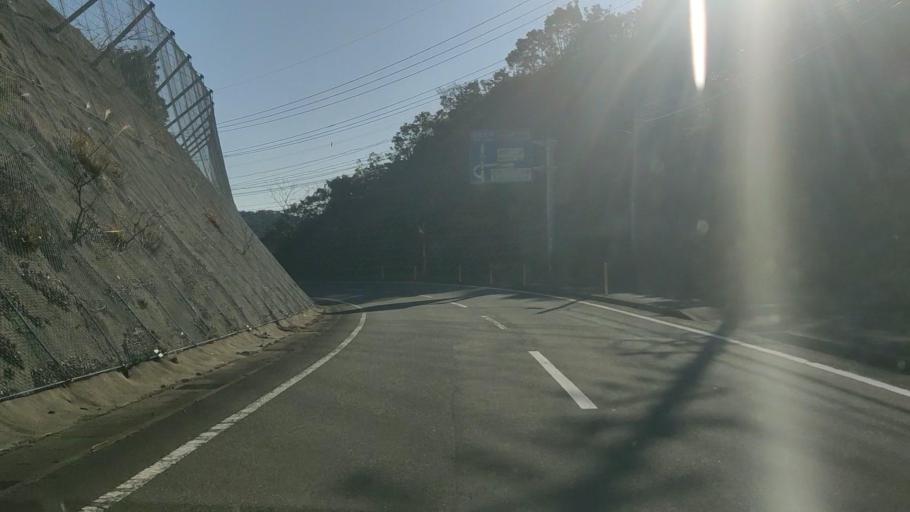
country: JP
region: Miyazaki
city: Nobeoka
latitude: 32.6759
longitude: 131.7778
